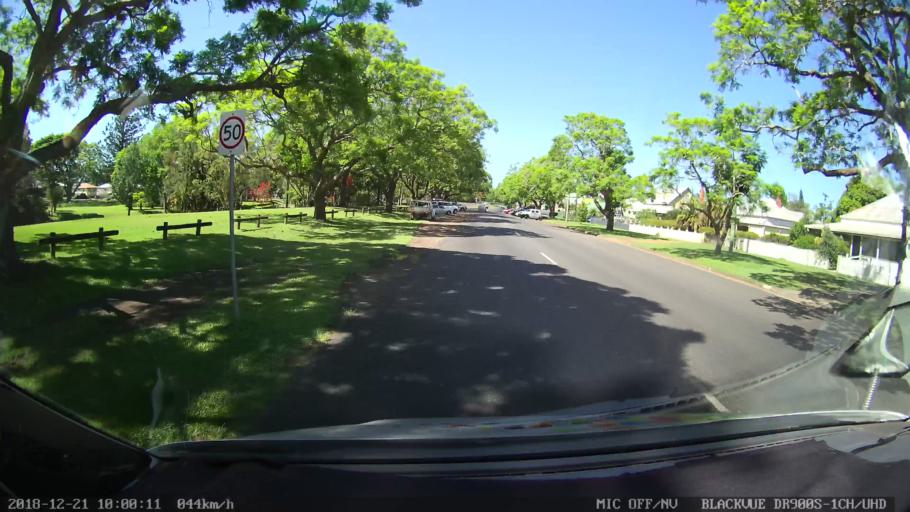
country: AU
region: New South Wales
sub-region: Clarence Valley
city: Grafton
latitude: -29.6826
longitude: 152.9273
